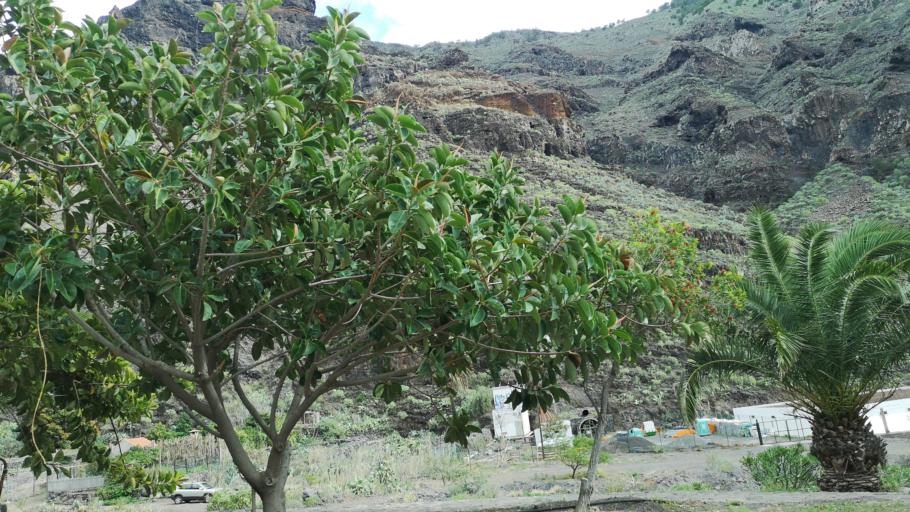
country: ES
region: Canary Islands
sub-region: Provincia de Santa Cruz de Tenerife
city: Alajero
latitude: 28.1015
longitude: -17.3290
